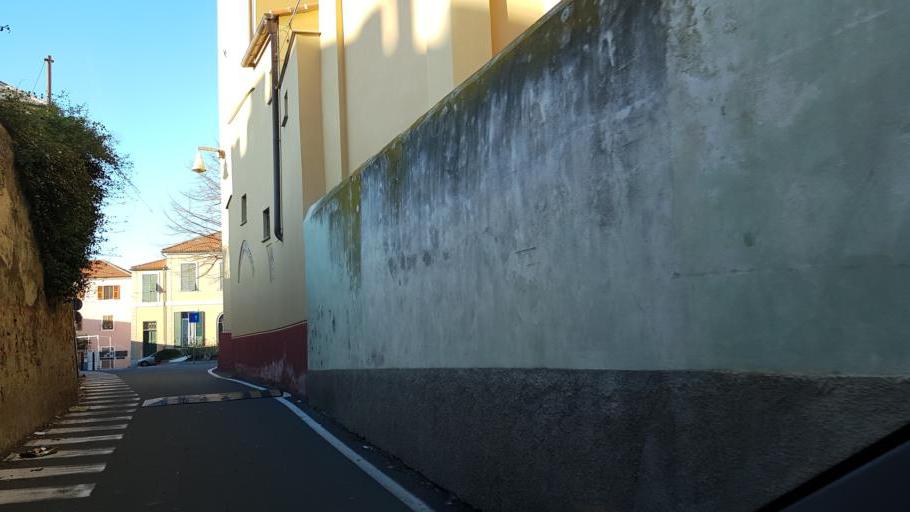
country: IT
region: Liguria
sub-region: Provincia di Savona
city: Savona
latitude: 44.2952
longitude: 8.4532
